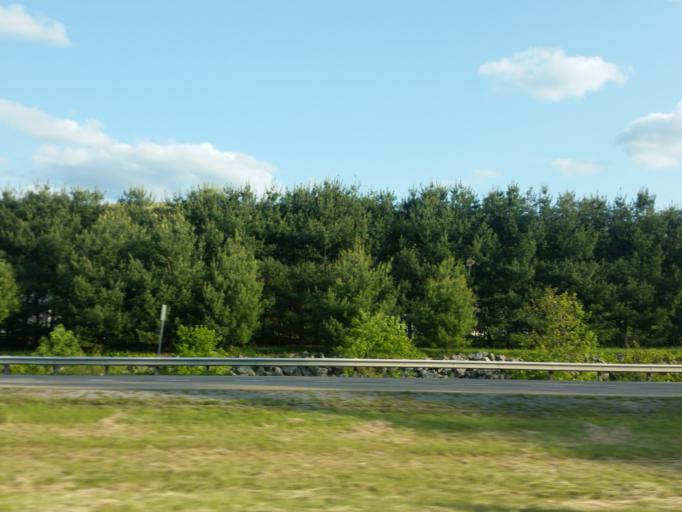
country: US
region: Virginia
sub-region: Tazewell County
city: Raven
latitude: 36.9802
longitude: -81.8651
